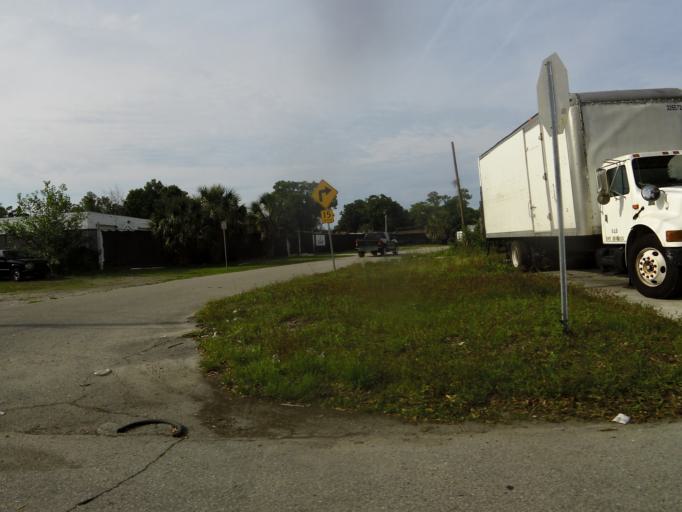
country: US
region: Florida
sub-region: Duval County
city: Jacksonville
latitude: 30.3360
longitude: -81.5978
